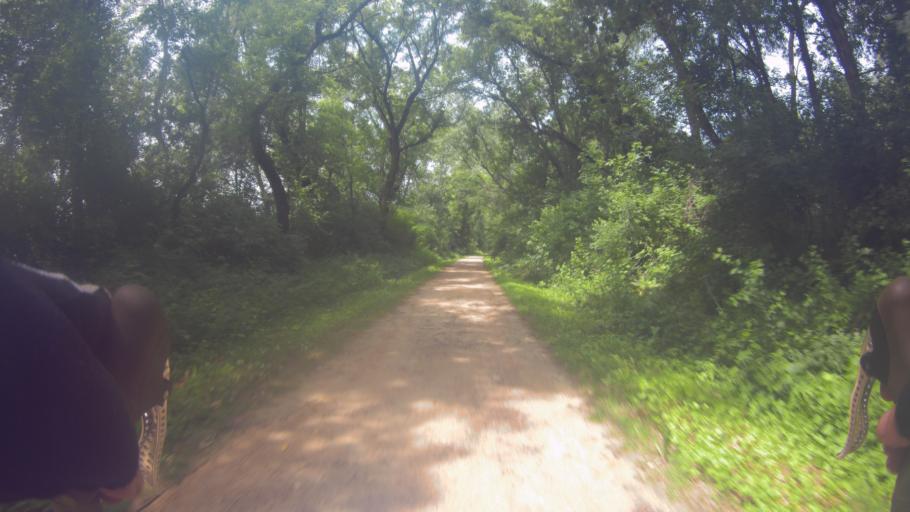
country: US
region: Wisconsin
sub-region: Dane County
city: Mount Horeb
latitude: 43.0170
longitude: -89.6856
